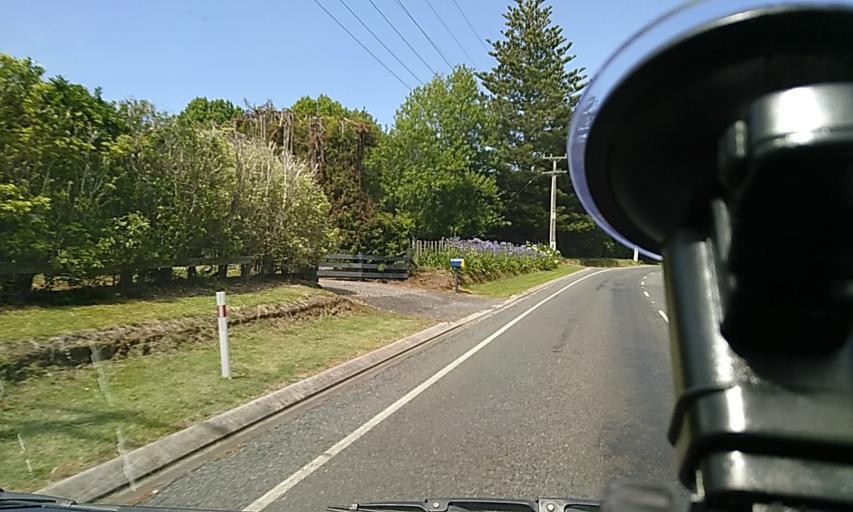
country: NZ
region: Bay of Plenty
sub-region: Western Bay of Plenty District
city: Waihi Beach
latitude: -37.4483
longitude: 175.9535
